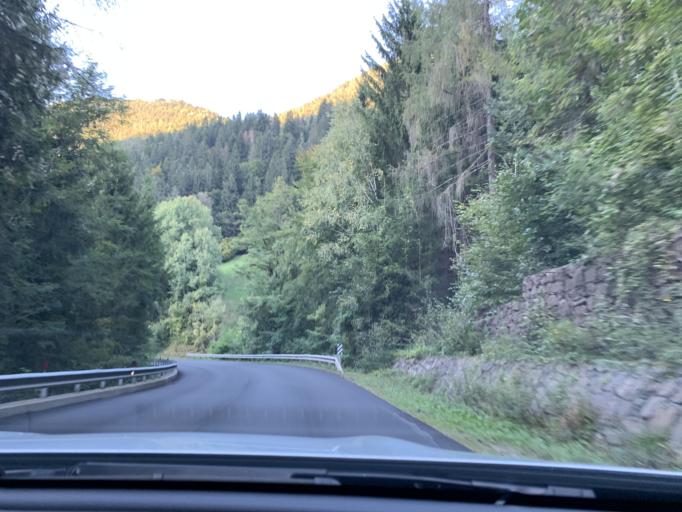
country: IT
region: Trentino-Alto Adige
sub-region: Bolzano
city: Nova Ponente
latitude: 46.4414
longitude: 11.4645
